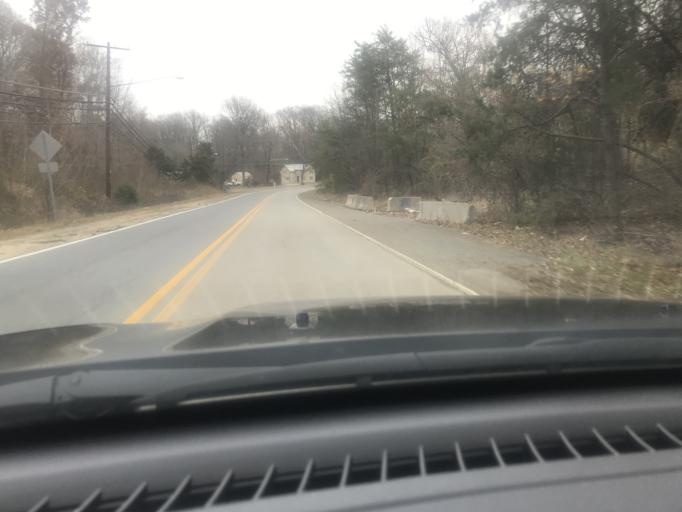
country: US
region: Maryland
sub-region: Prince George's County
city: Friendly
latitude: 38.7744
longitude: -76.9710
